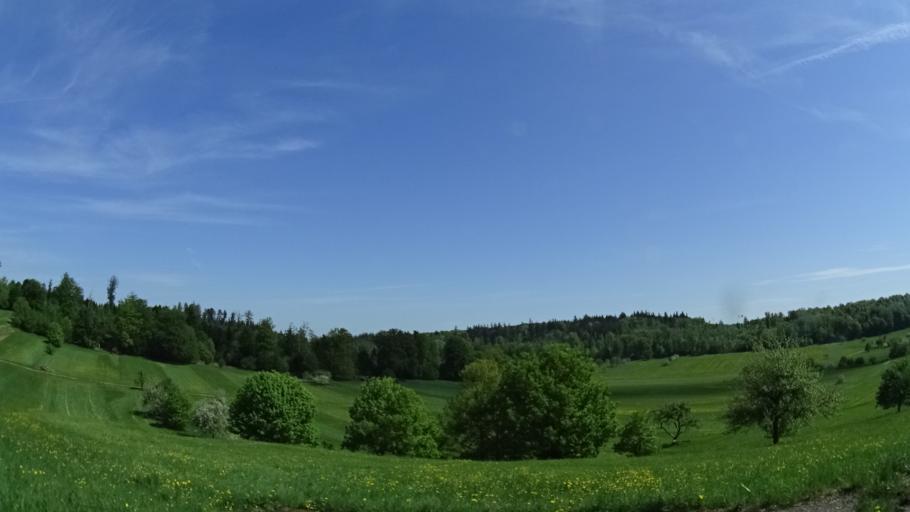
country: DE
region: Baden-Wuerttemberg
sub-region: Karlsruhe Region
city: Bad Herrenalb
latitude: 48.8278
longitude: 8.4119
